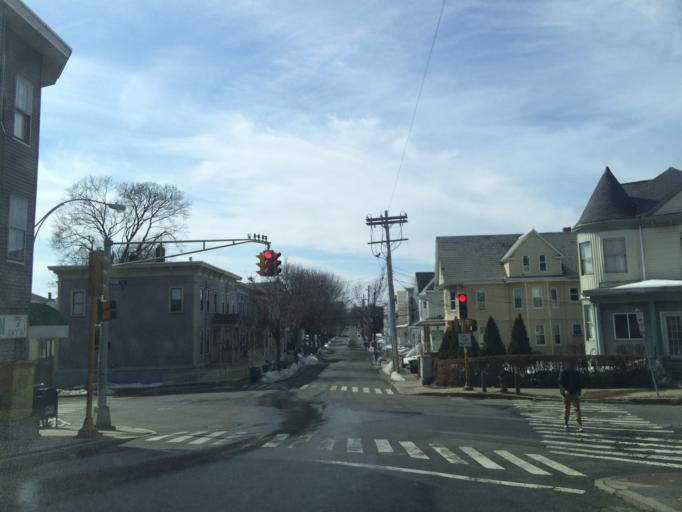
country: US
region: Massachusetts
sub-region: Middlesex County
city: Somerville
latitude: 42.3927
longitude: -71.1004
